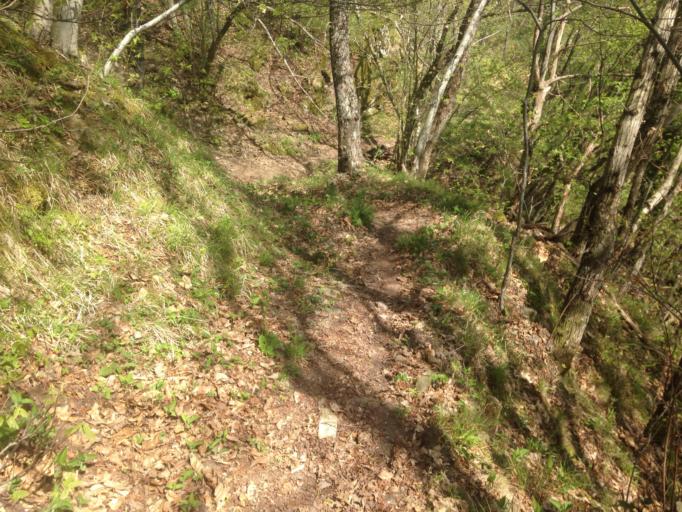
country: IT
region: Emilia-Romagna
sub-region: Provincia di Bologna
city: Lizzano in Belvedere
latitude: 44.1556
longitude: 10.8917
